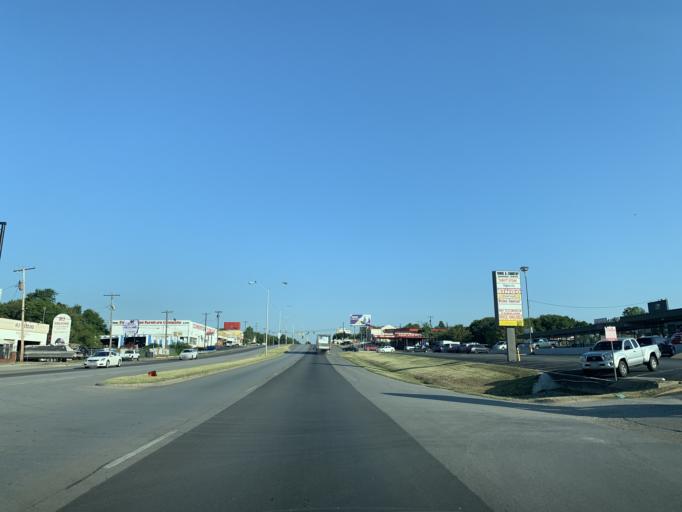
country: US
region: Texas
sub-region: Tarrant County
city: River Oaks
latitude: 32.7873
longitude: -97.3853
